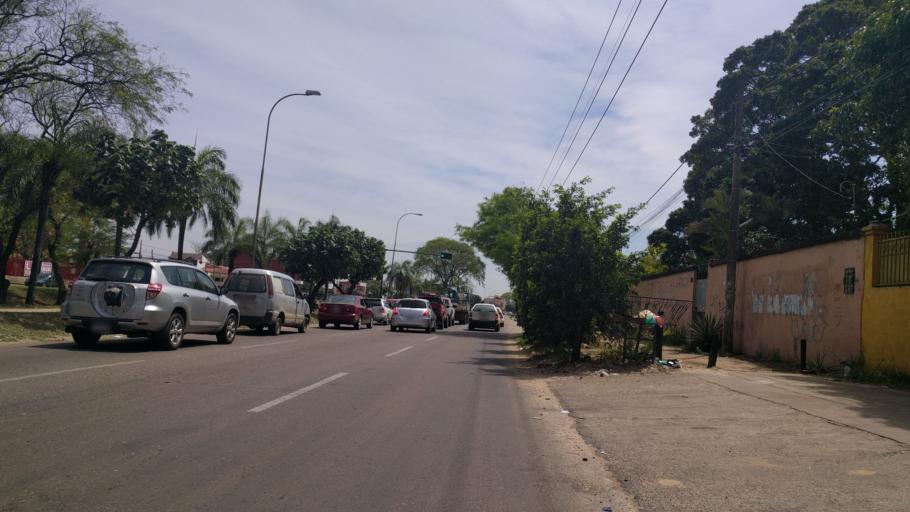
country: BO
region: Santa Cruz
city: Santa Cruz de la Sierra
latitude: -17.8068
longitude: -63.2119
